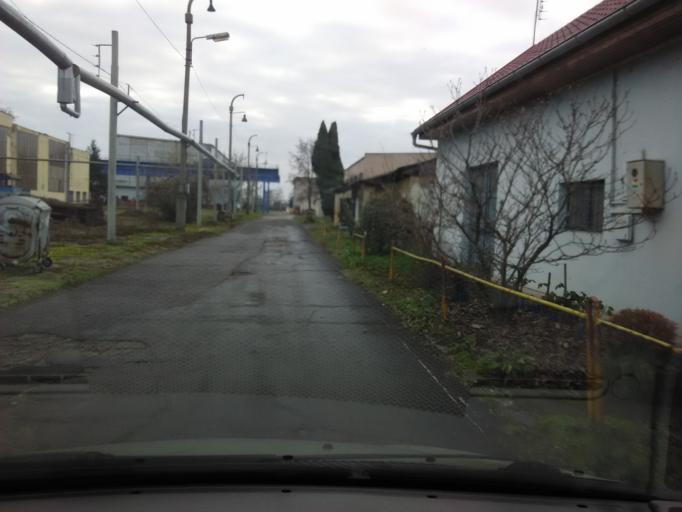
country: SK
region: Nitriansky
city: Tlmace
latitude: 48.2940
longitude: 18.5393
